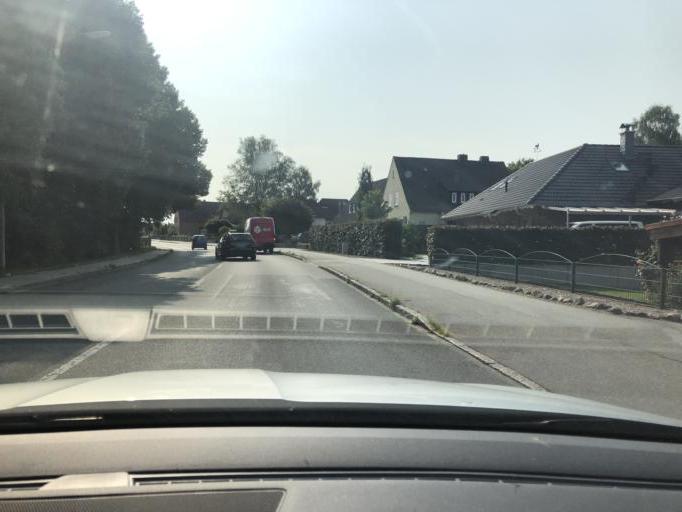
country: DE
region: Schleswig-Holstein
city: Gross Gronau
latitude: 53.8076
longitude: 10.7486
